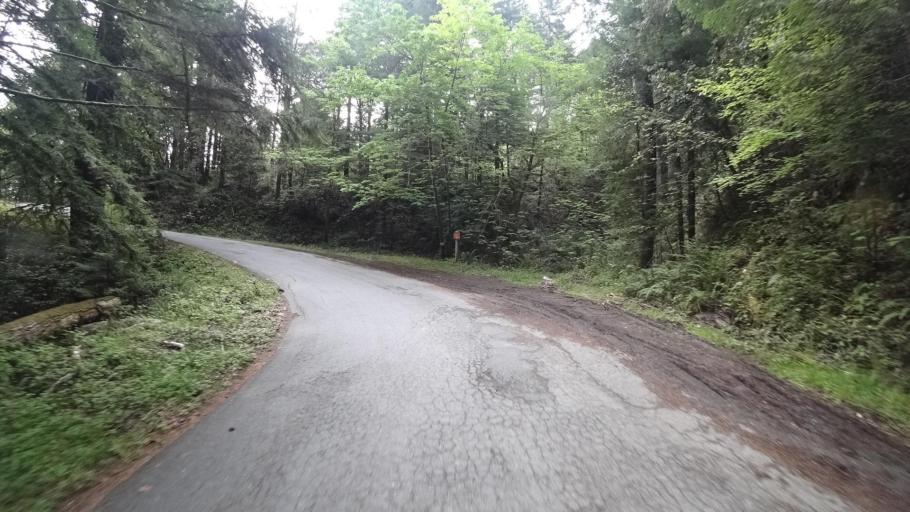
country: US
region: California
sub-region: Humboldt County
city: Redway
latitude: 40.3388
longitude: -123.9137
